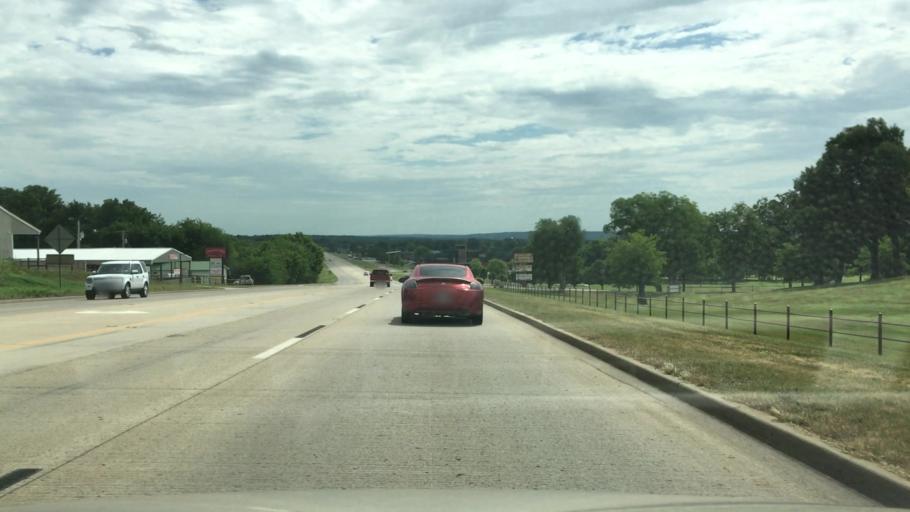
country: US
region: Oklahoma
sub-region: Cherokee County
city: Park Hill
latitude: 35.8507
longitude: -94.9981
